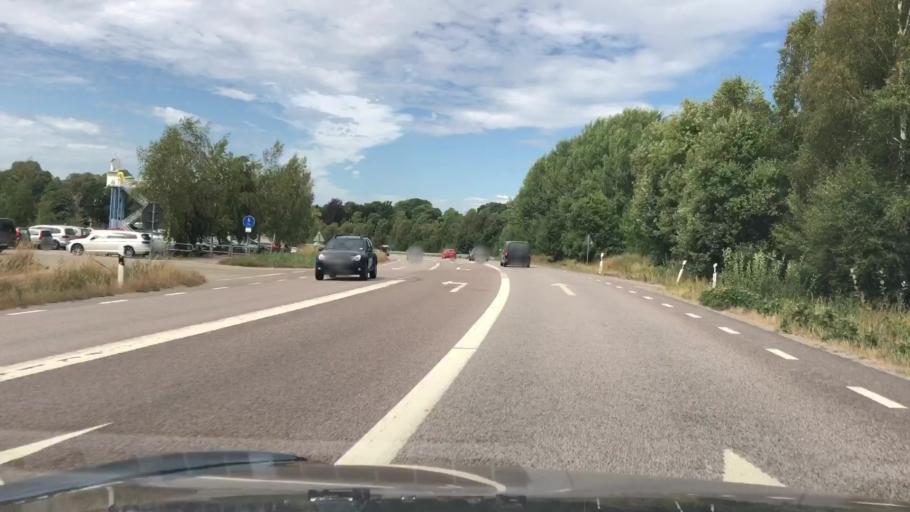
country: SE
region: Blekinge
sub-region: Karlskrona Kommun
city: Rodeby
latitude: 56.1959
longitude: 15.6967
